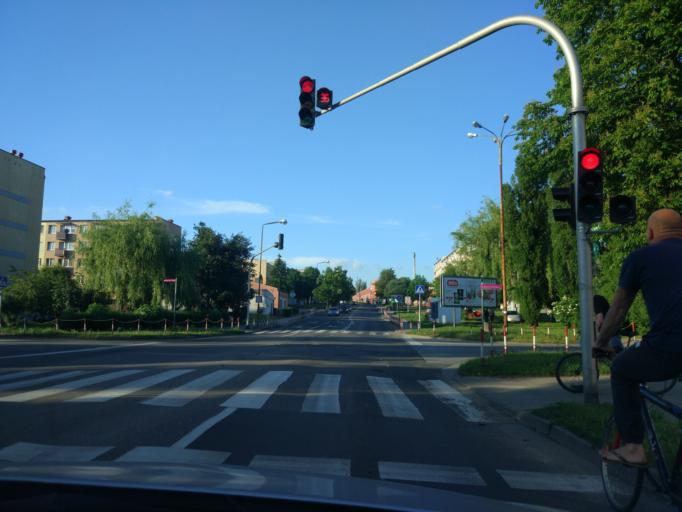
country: PL
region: Lodz Voivodeship
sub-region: Powiat kutnowski
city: Kutno
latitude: 52.2271
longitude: 19.3662
